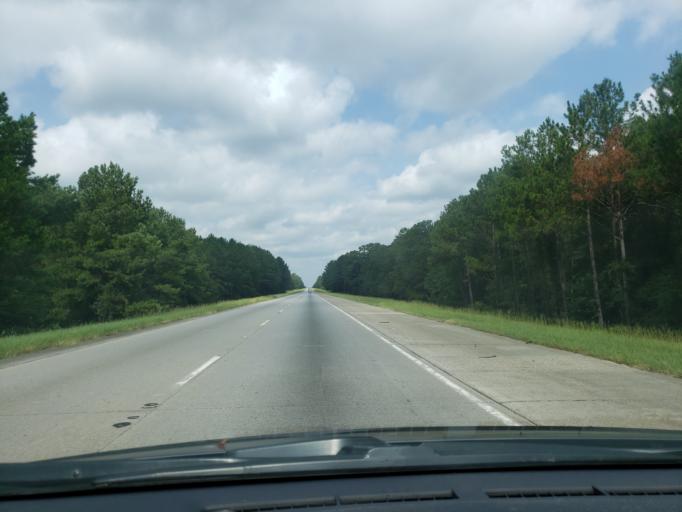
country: US
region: Georgia
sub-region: Emanuel County
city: Swainsboro
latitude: 32.4091
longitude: -82.3520
